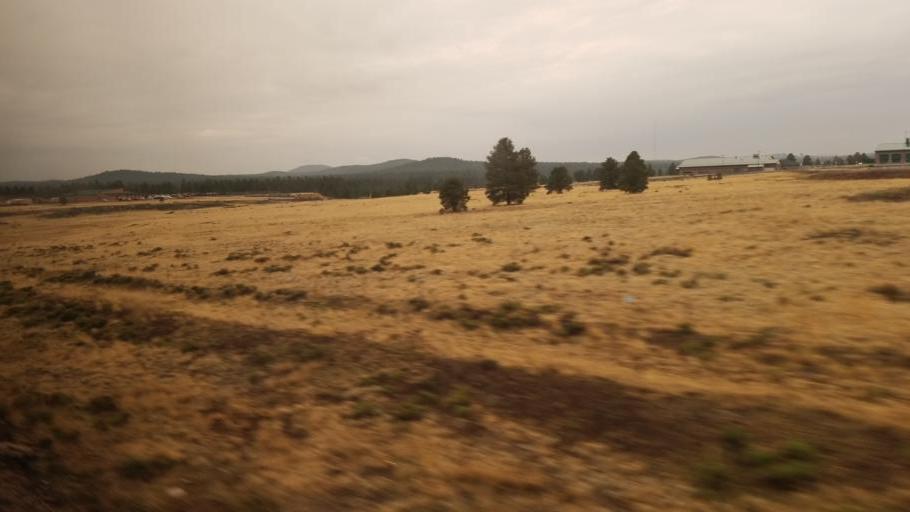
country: US
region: Arizona
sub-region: Coconino County
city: Parks
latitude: 35.2316
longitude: -111.8198
